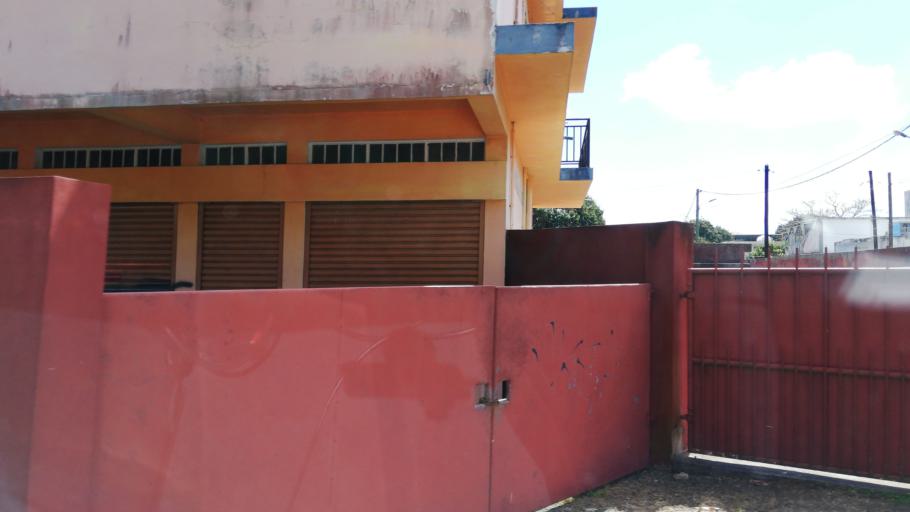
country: MU
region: Moka
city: Moka
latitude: -20.2229
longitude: 57.4731
